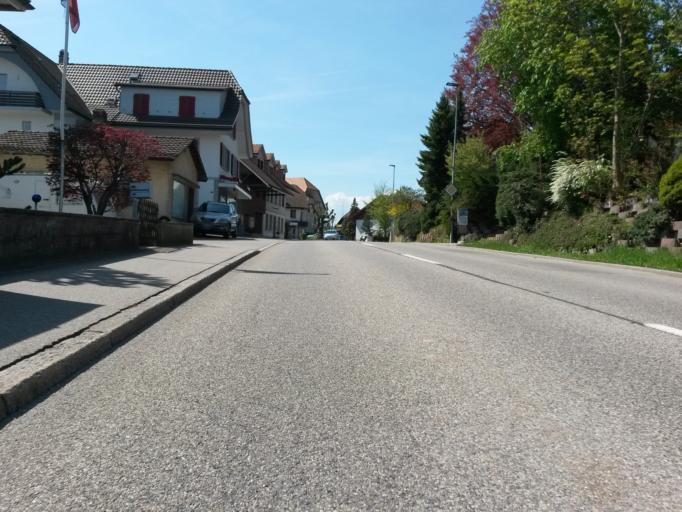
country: CH
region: Bern
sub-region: Oberaargau
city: Seeberg
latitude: 47.1808
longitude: 7.6619
